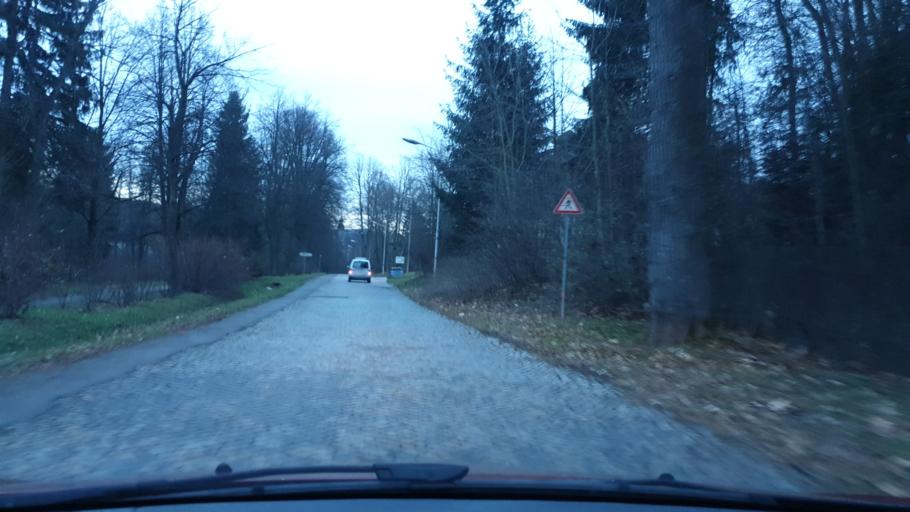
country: DE
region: Saxony
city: Schneeberg
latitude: 50.6041
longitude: 12.6398
